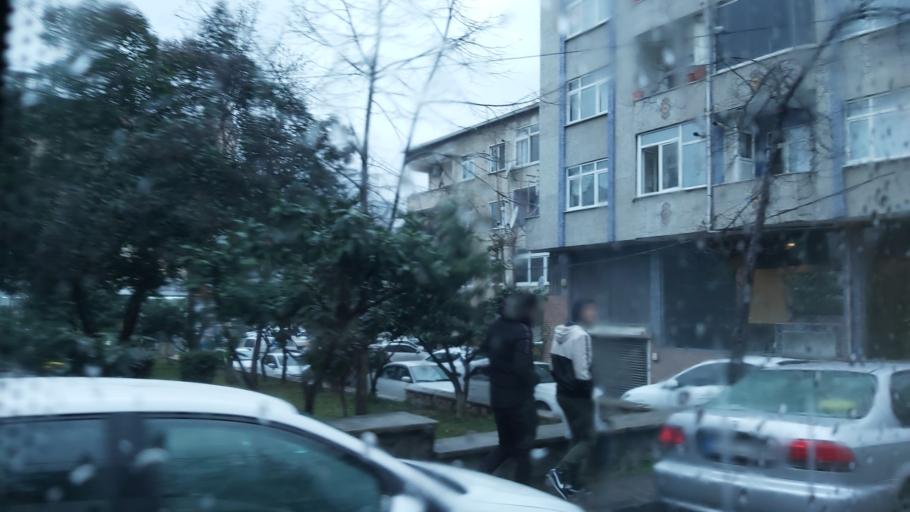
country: TR
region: Istanbul
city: Sisli
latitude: 41.0850
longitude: 28.9854
